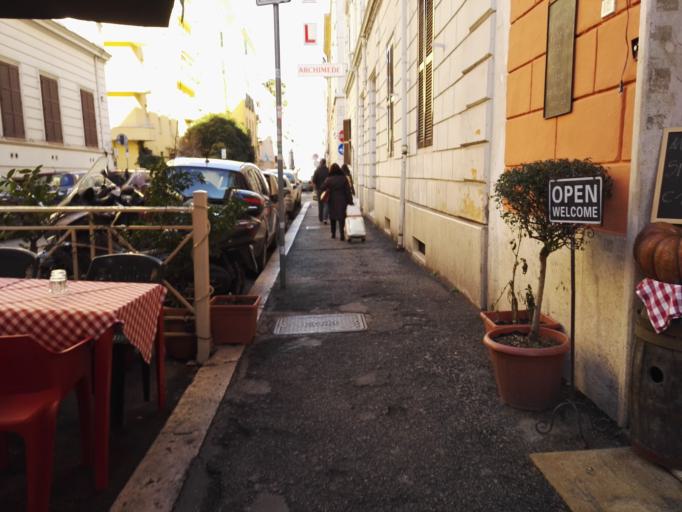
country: IT
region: Latium
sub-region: Citta metropolitana di Roma Capitale
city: Rome
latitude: 41.9025
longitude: 12.5038
